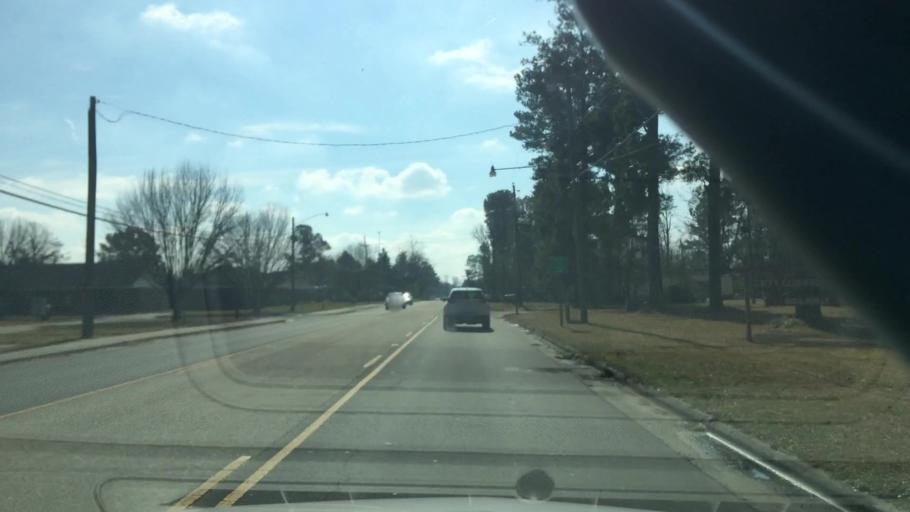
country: US
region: North Carolina
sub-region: Duplin County
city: Beulaville
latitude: 34.9202
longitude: -77.7746
